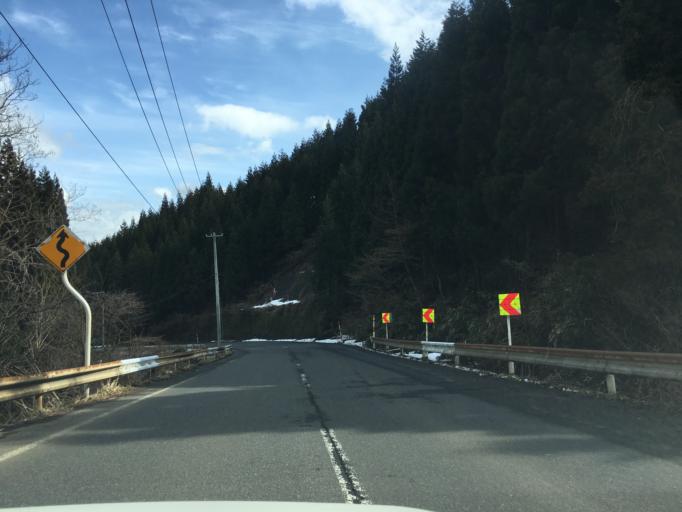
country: JP
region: Akita
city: Odate
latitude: 40.1923
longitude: 140.5250
